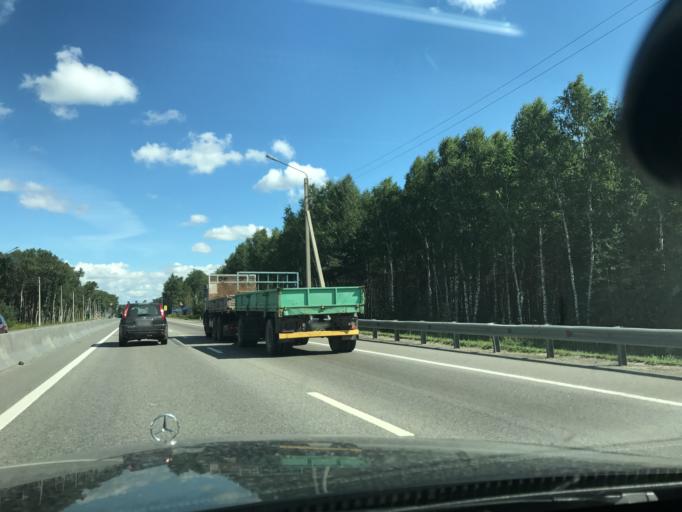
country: RU
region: Nizjnij Novgorod
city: Babino
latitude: 56.3045
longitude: 43.6263
